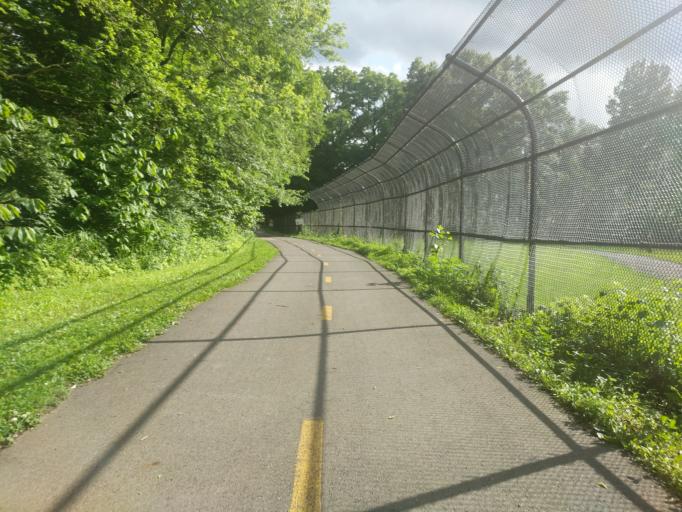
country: US
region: Ohio
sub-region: Franklin County
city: Minerva Park
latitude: 40.0452
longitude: -82.9329
